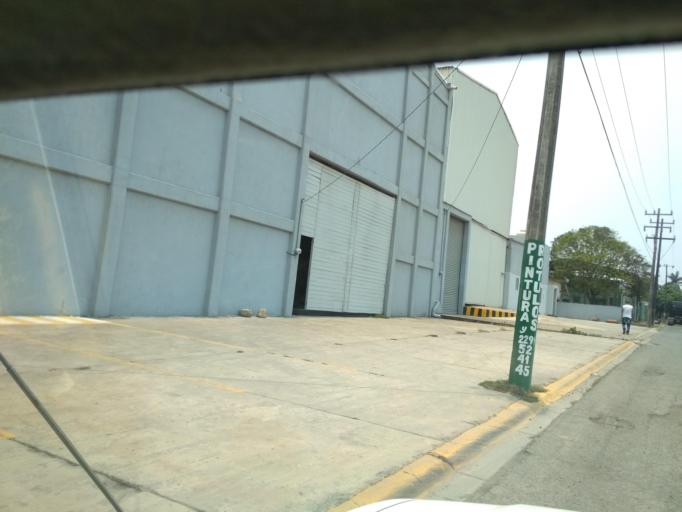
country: MX
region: Veracruz
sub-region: Veracruz
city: Lomas de Rio Medio Cuatro
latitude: 19.1691
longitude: -96.2371
